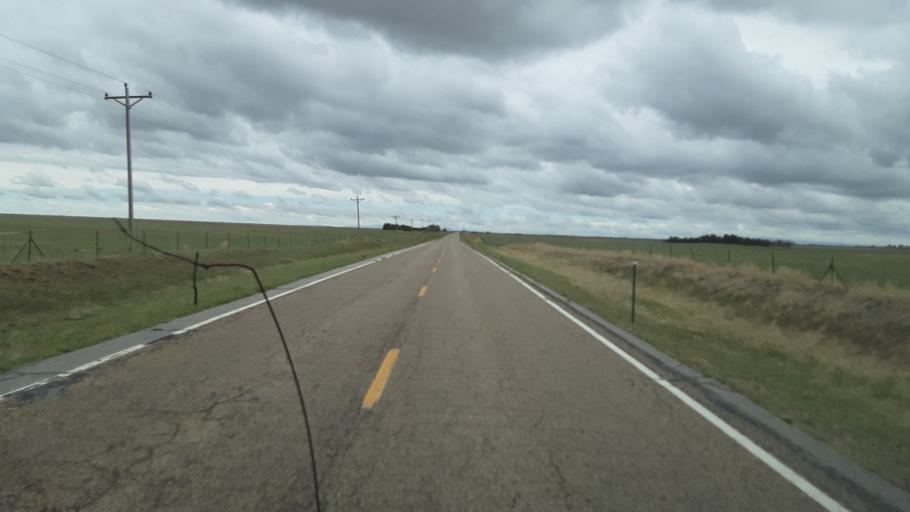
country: US
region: Colorado
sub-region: El Paso County
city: Ellicott
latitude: 38.8398
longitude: -103.9584
